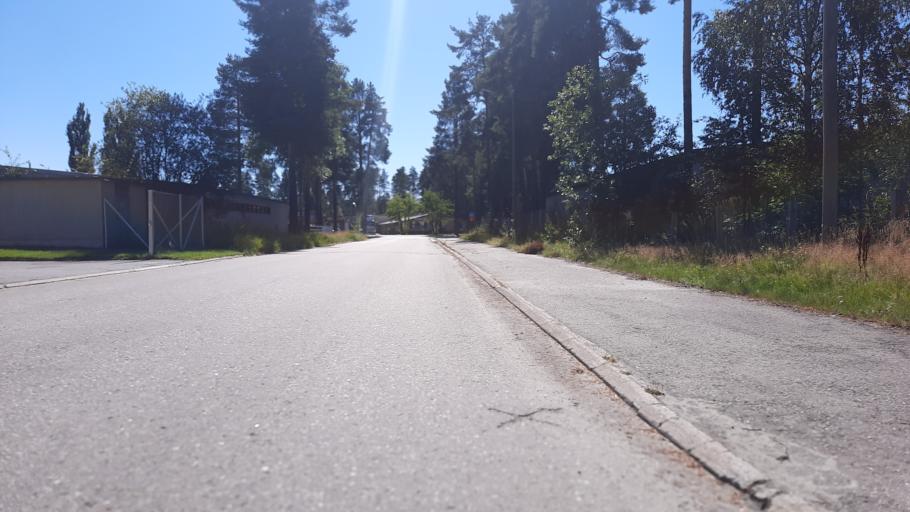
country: FI
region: North Karelia
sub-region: Joensuu
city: Joensuu
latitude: 62.6189
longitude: 29.7397
